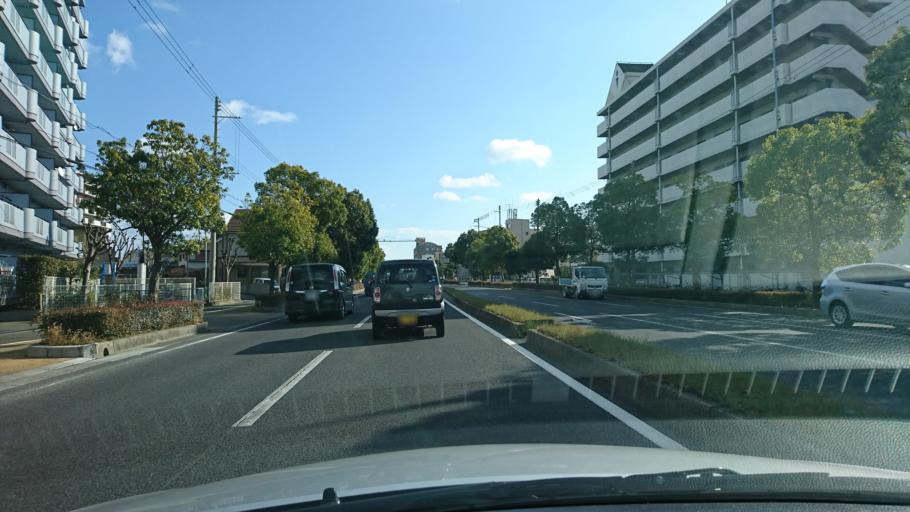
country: JP
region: Hyogo
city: Kakogawacho-honmachi
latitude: 34.7039
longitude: 134.8878
